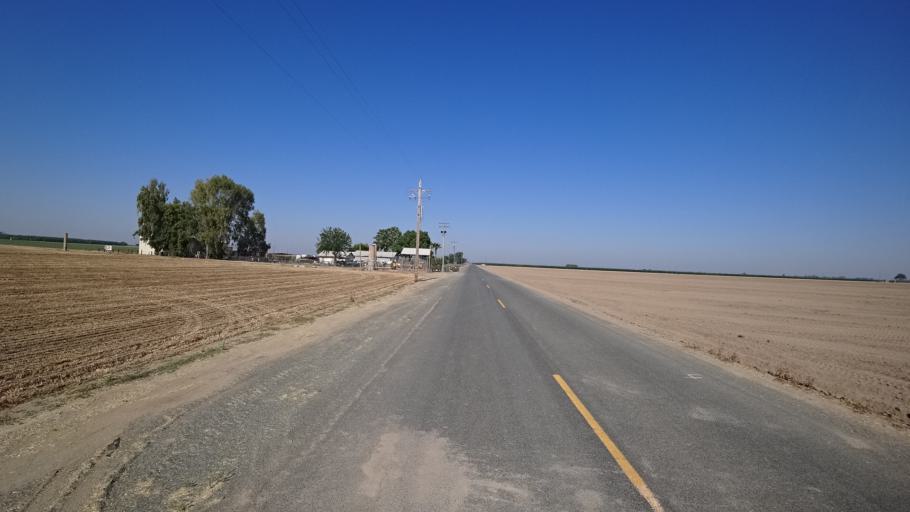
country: US
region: California
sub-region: Kings County
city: Hanford
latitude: 36.3867
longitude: -119.5507
